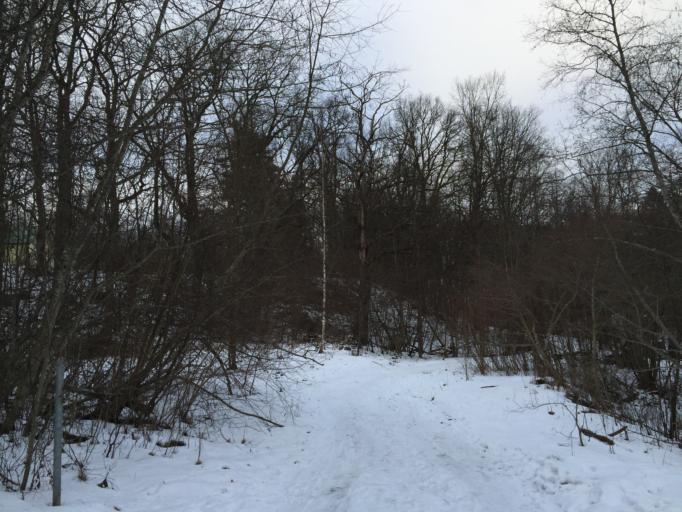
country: LV
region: Seja
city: Loja
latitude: 57.1313
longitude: 24.6659
